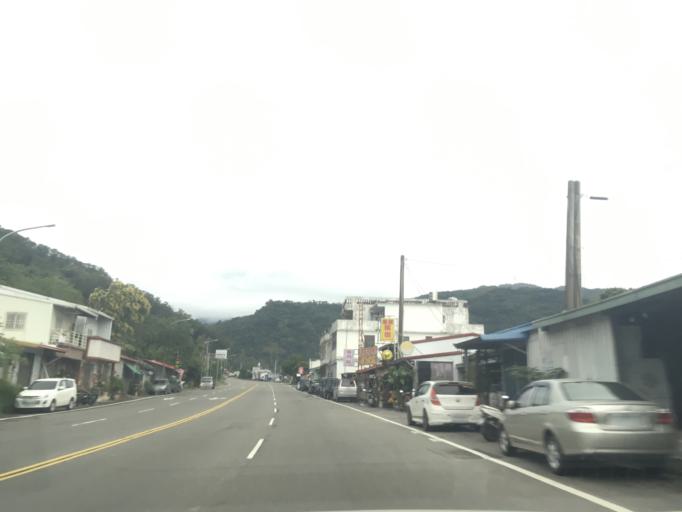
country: TW
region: Taiwan
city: Taitung City
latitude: 22.7570
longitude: 121.0524
